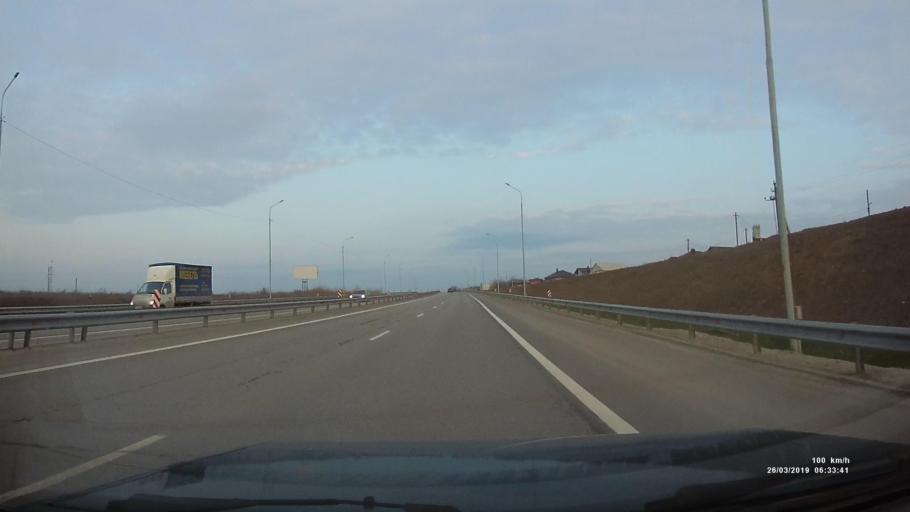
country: RU
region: Rostov
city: Chaltyr
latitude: 47.2731
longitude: 39.4862
